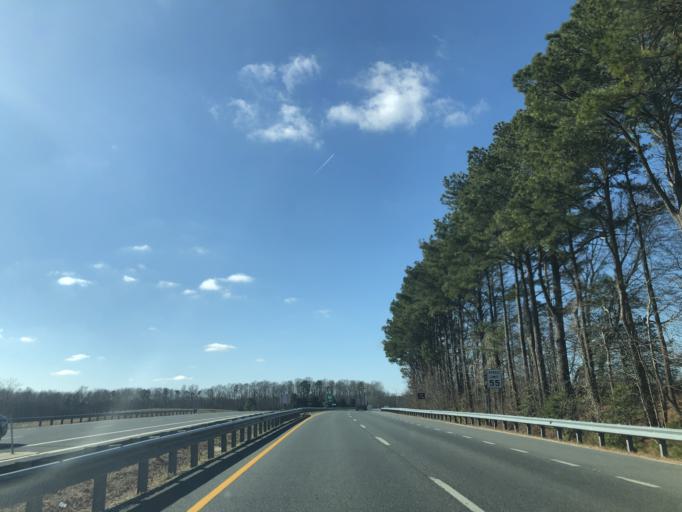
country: US
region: Maryland
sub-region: Worcester County
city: Berlin
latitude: 38.2580
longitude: -75.2594
